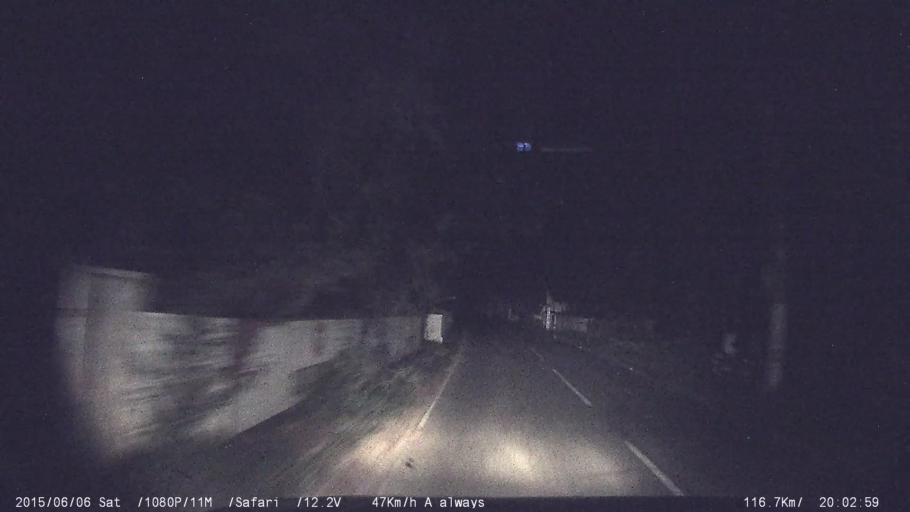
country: IN
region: Kerala
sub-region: Kottayam
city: Palackattumala
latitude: 9.6517
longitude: 76.6119
